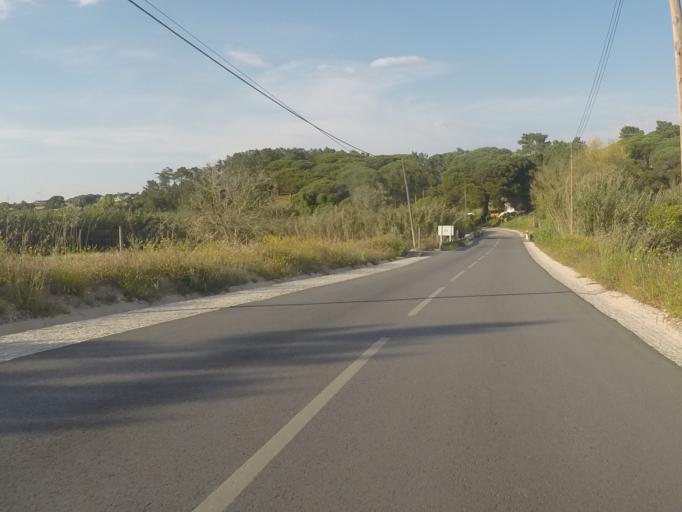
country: PT
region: Setubal
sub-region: Sesimbra
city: Sesimbra
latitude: 38.4728
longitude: -9.1684
